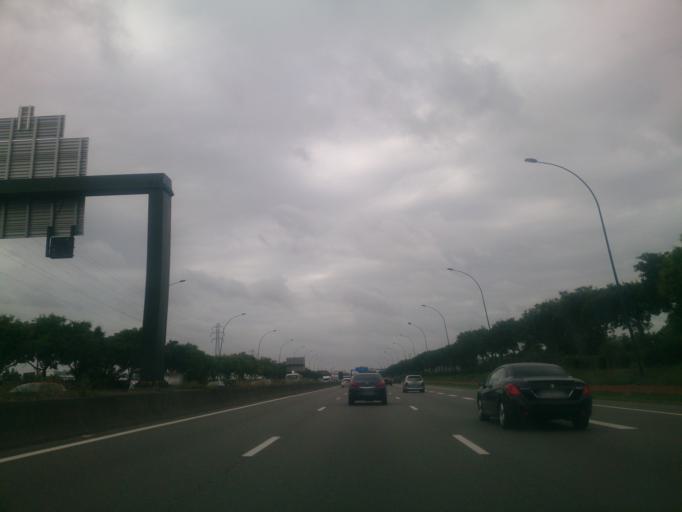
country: FR
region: Midi-Pyrenees
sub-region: Departement de la Haute-Garonne
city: Portet-sur-Garonne
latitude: 43.5604
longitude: 1.4156
